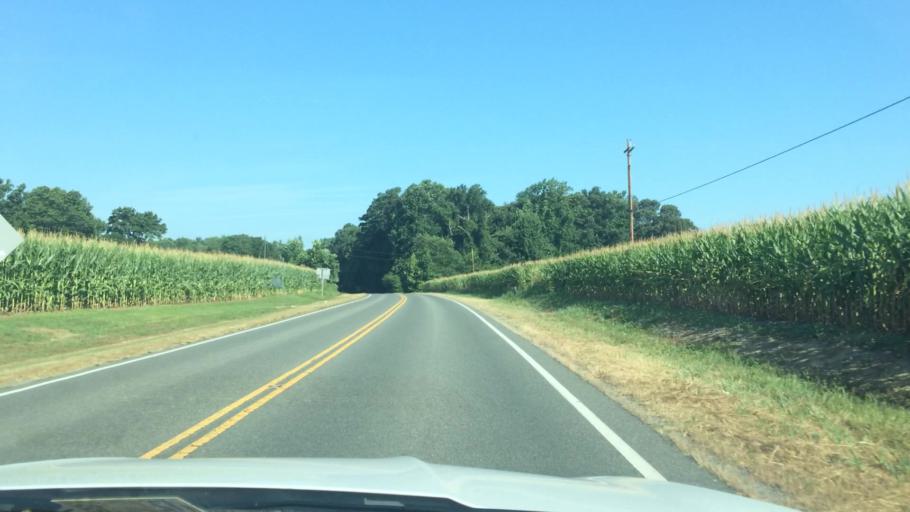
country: US
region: Virginia
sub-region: Lancaster County
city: Lancaster
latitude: 37.7965
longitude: -76.5224
